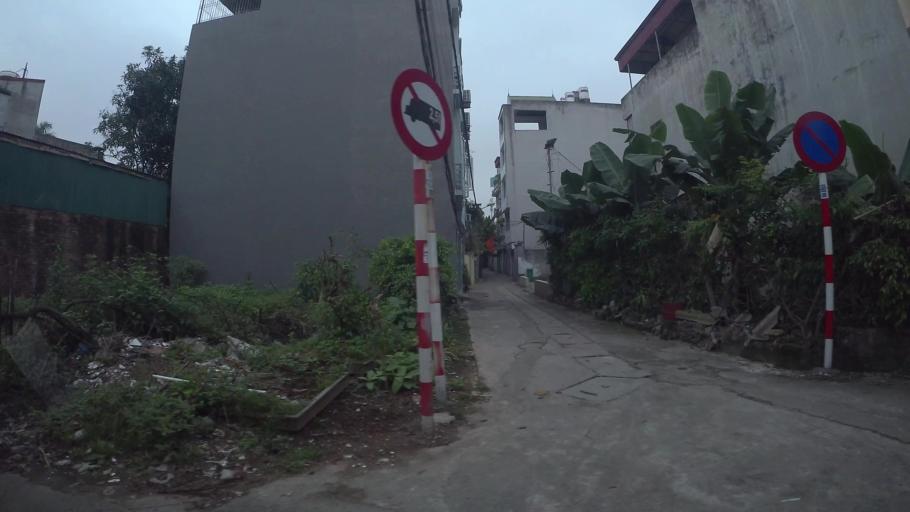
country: VN
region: Hung Yen
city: Van Giang
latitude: 20.9717
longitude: 105.8927
